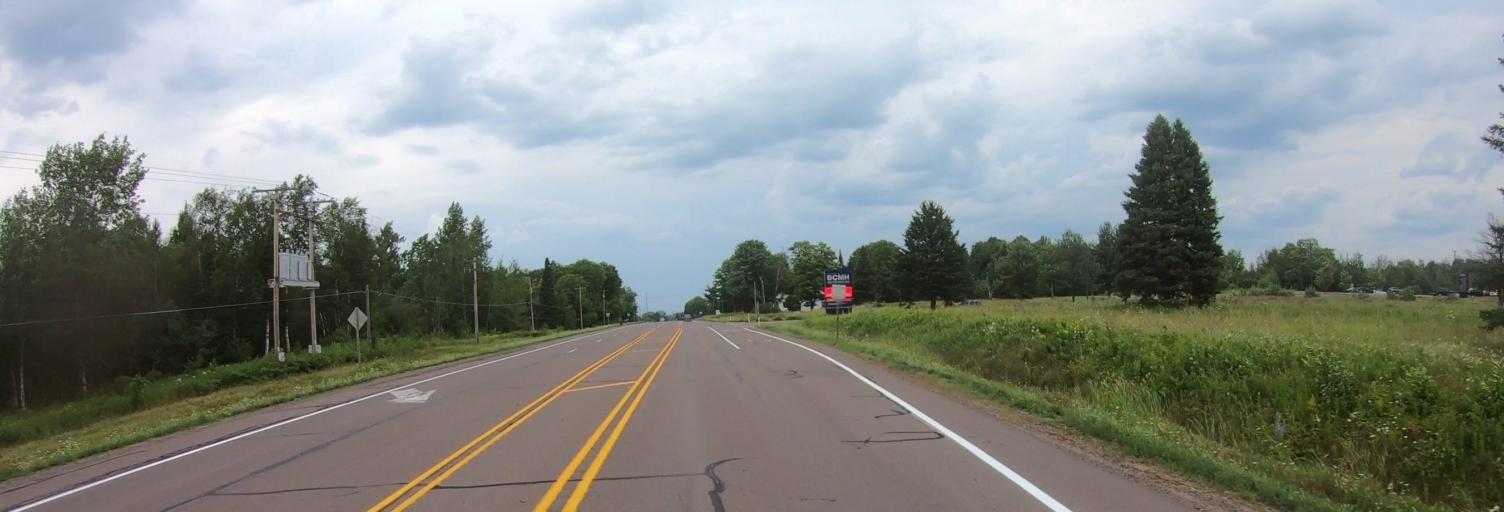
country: US
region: Michigan
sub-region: Baraga County
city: L'Anse
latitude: 46.7315
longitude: -88.4281
